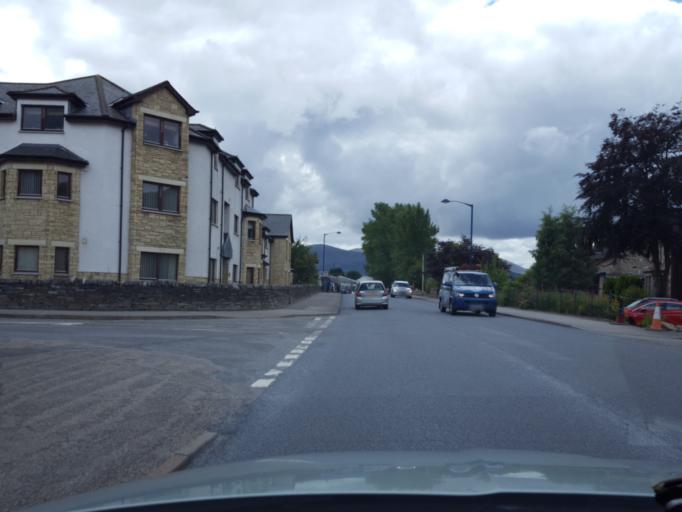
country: GB
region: Scotland
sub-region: Highland
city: Aviemore
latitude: 57.1944
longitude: -3.8291
